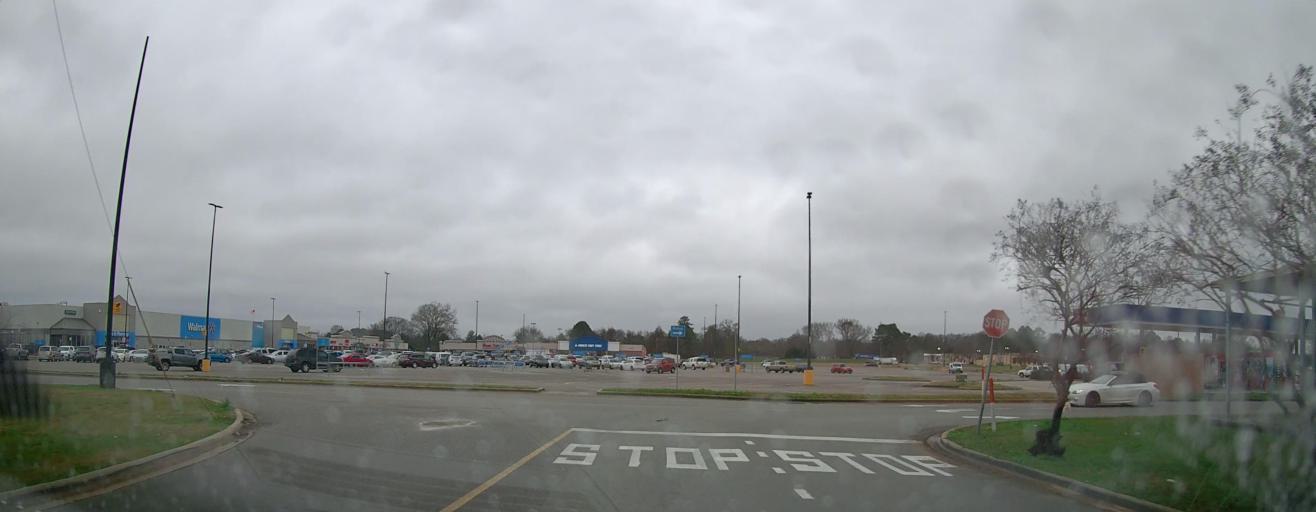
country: US
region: Alabama
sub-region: Morgan County
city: Flint City
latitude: 34.5579
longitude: -86.9977
